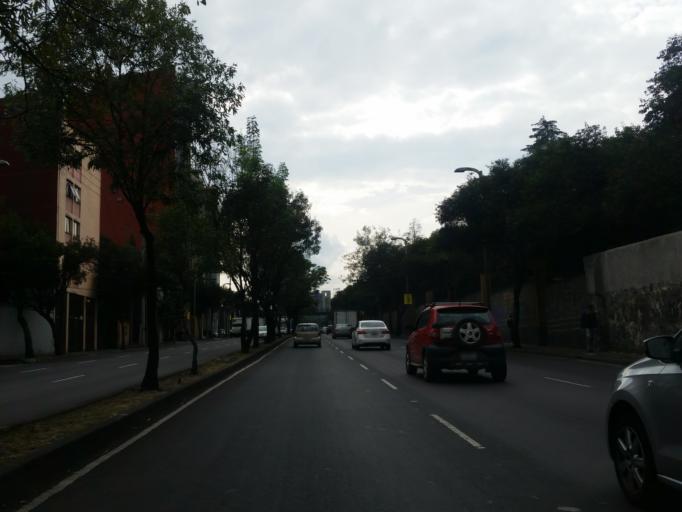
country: MX
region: Mexico City
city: Polanco
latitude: 19.4022
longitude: -99.2088
